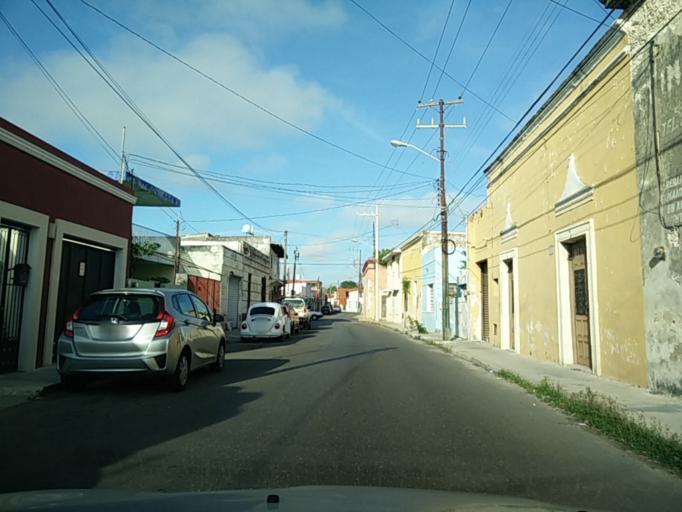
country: MX
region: Yucatan
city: Merida
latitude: 20.9673
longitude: -89.6338
